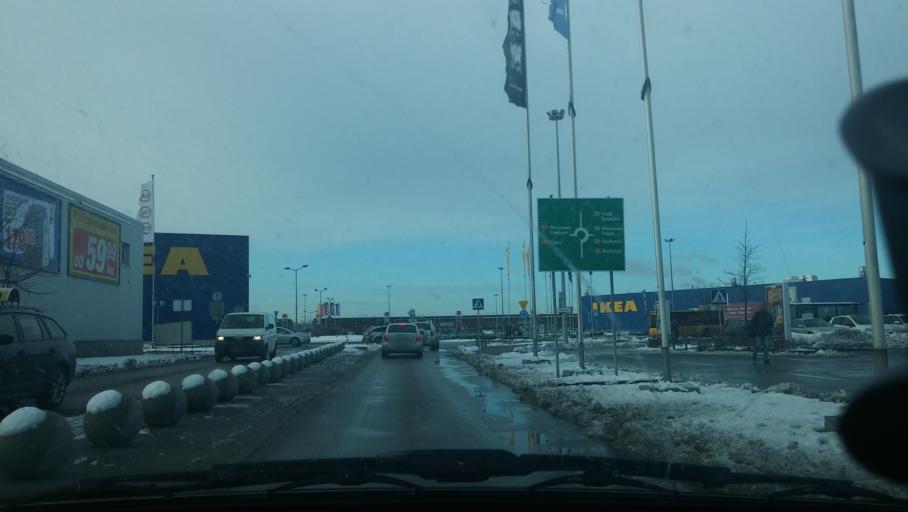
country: PL
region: Masovian Voivodeship
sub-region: Powiat wolominski
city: Zabki
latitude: 52.3044
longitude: 21.0862
